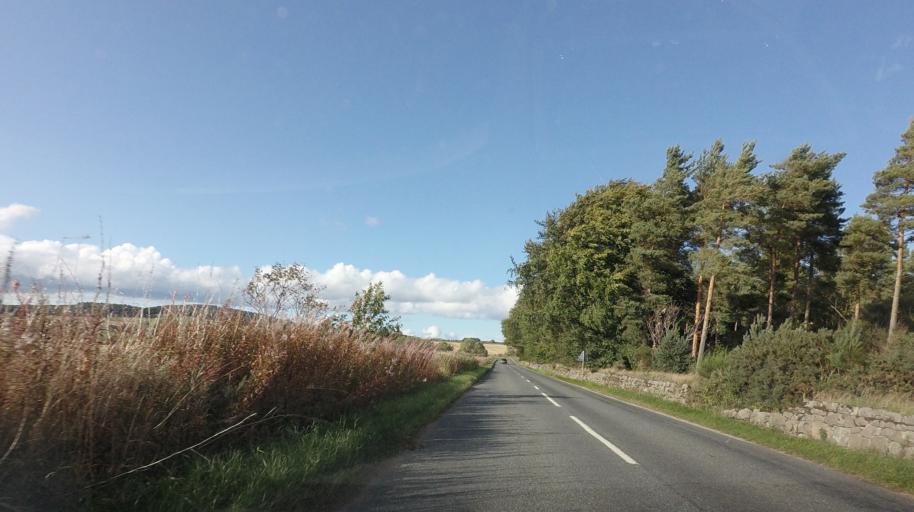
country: GB
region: Scotland
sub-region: Aberdeenshire
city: Banchory
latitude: 57.1314
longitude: -2.4277
